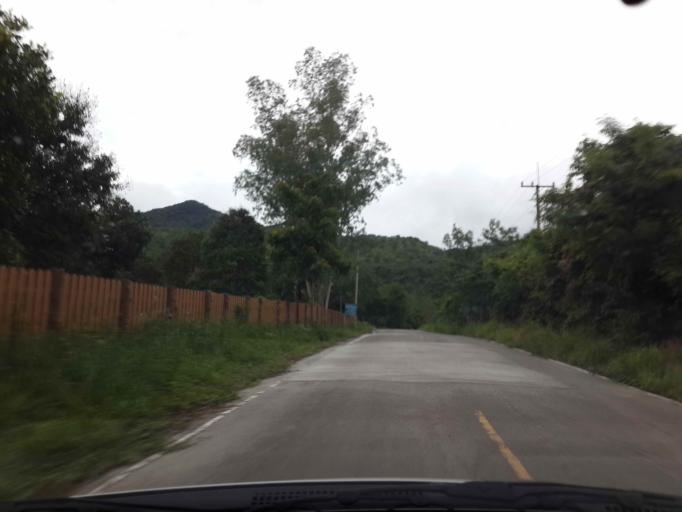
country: TH
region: Ratchaburi
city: Suan Phueng
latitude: 13.5861
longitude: 99.2173
